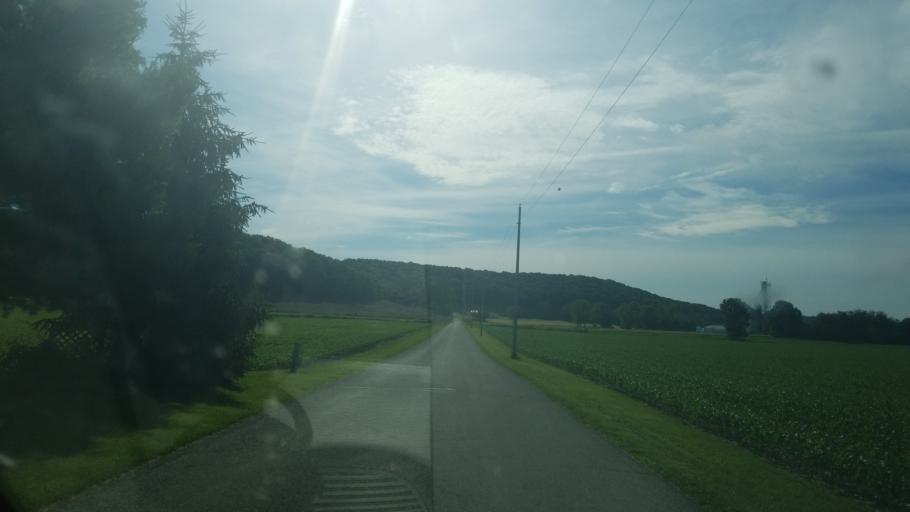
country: US
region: Ohio
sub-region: Licking County
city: Utica
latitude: 40.2088
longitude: -82.4340
